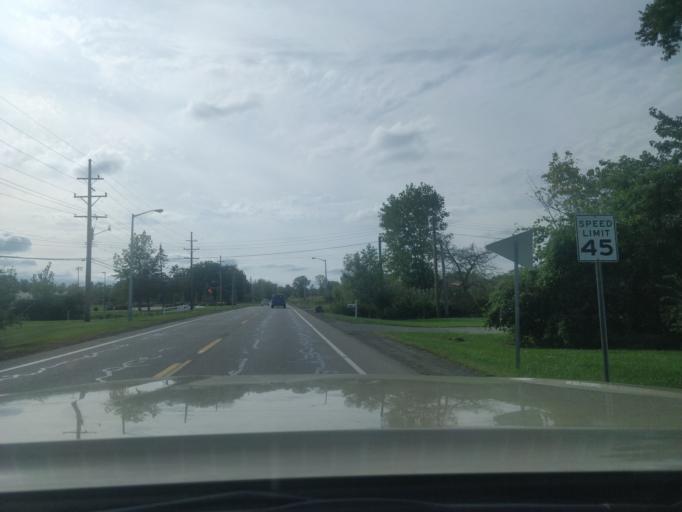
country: US
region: Michigan
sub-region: Wayne County
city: Woodhaven
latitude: 42.1531
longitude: -83.2606
